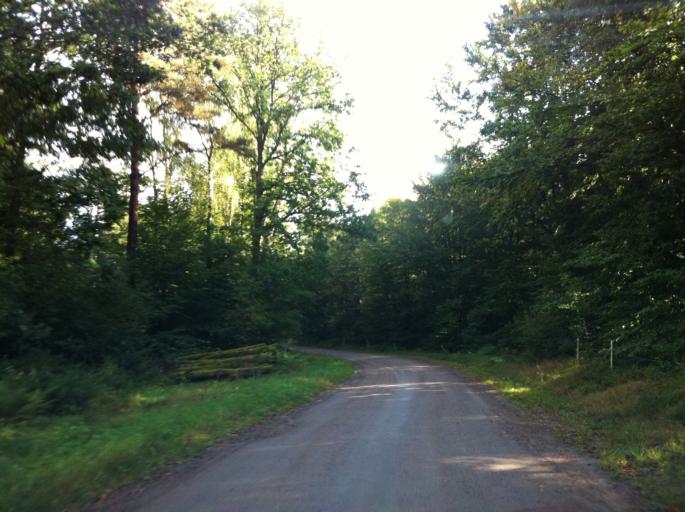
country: SE
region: Skane
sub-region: Hassleholms Kommun
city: Sosdala
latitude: 56.1278
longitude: 13.5911
